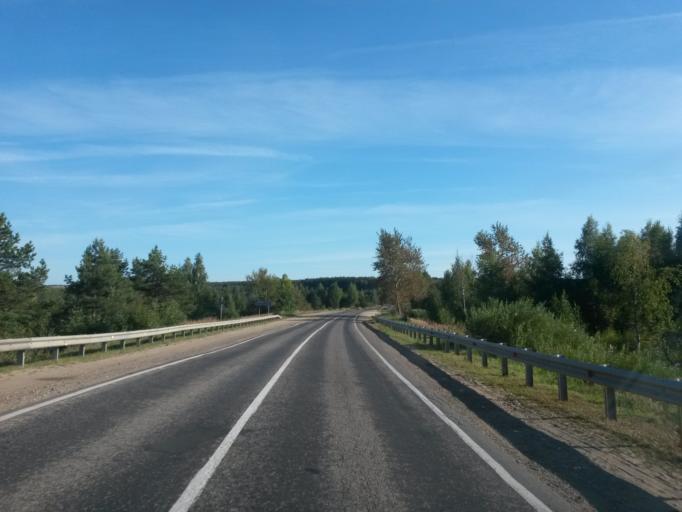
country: RU
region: Jaroslavl
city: Yaroslavl
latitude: 57.5145
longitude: 39.8961
